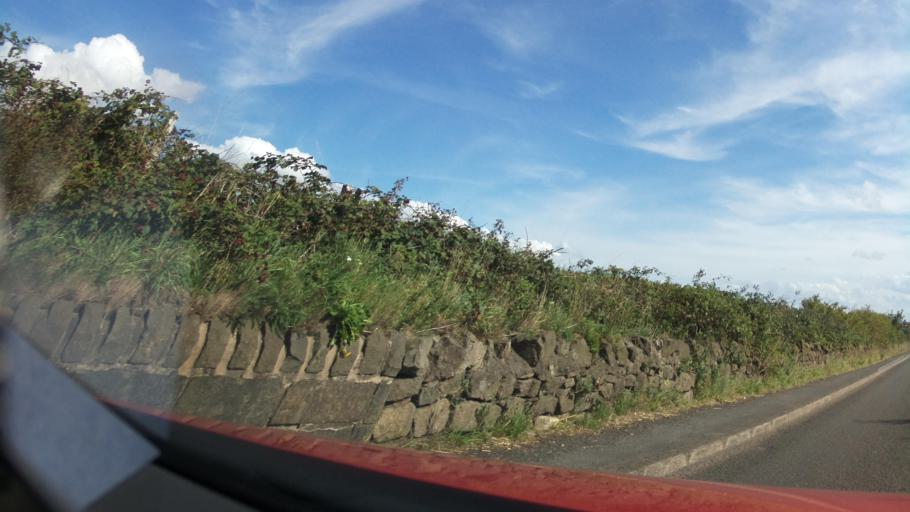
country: GB
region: Scotland
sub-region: Stirling
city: Plean
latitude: 56.0753
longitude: -3.8892
